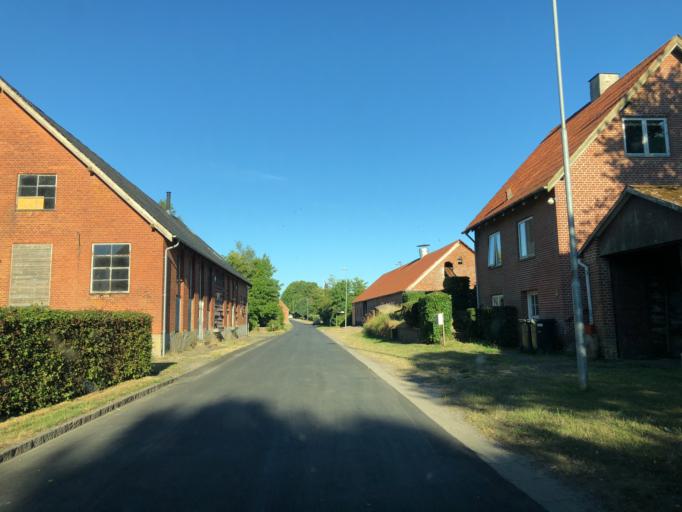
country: DK
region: Central Jutland
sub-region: Horsens Kommune
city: Horsens
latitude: 55.9626
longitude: 9.8204
